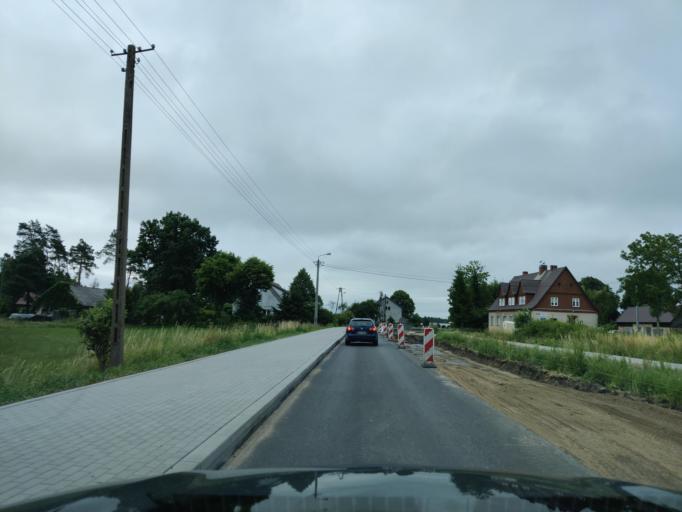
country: PL
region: Warmian-Masurian Voivodeship
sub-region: Powiat szczycienski
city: Rozogi
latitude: 53.4758
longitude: 21.3673
